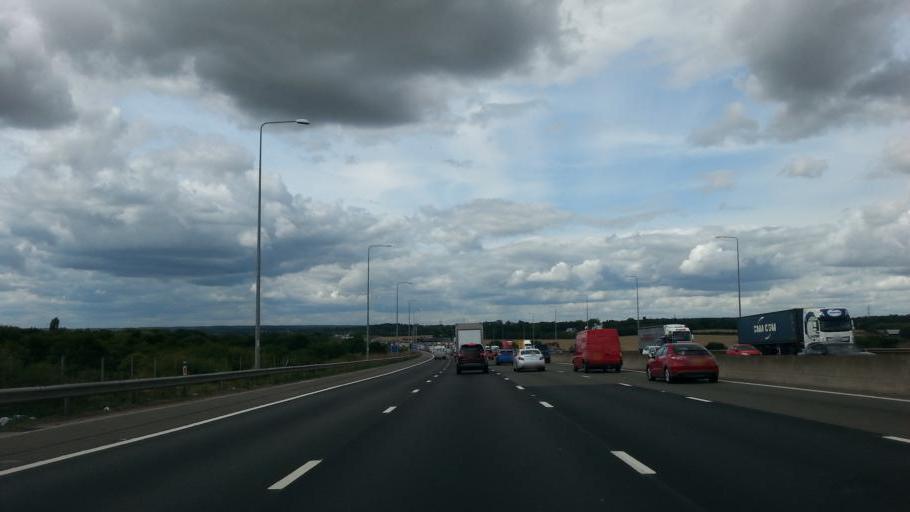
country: GB
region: England
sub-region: Greater London
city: Collier Row
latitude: 51.6501
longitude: 0.1983
